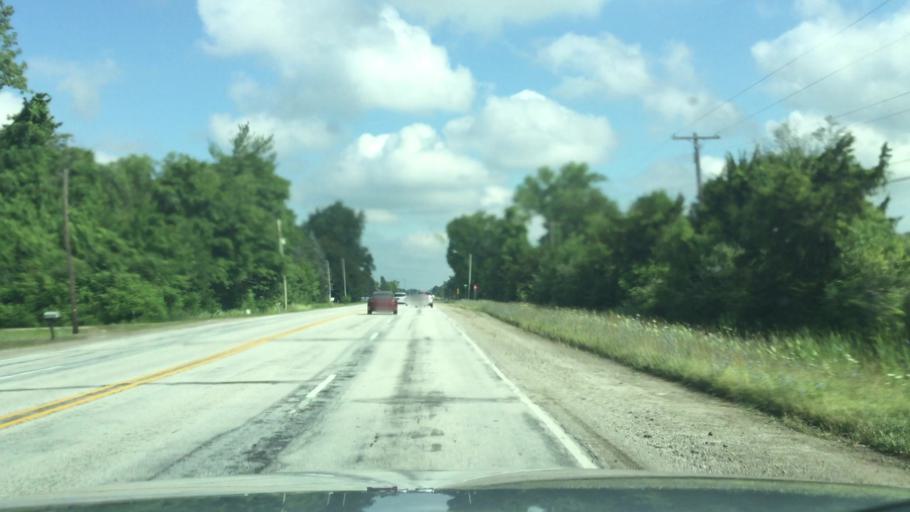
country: US
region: Michigan
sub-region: Saginaw County
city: Birch Run
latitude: 43.2273
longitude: -83.7520
